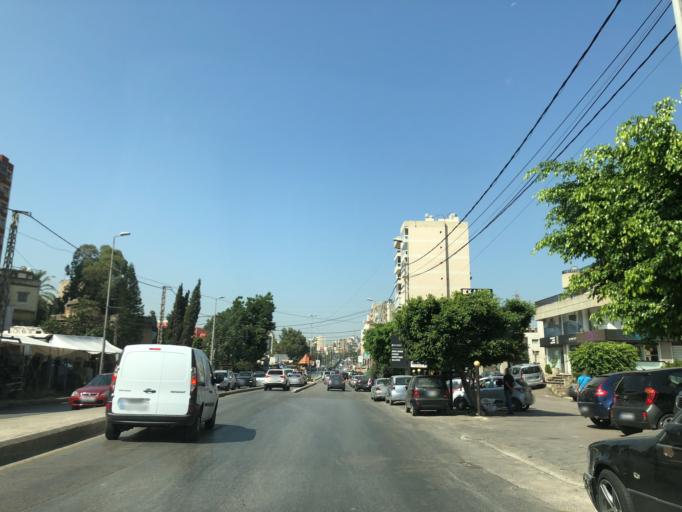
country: LB
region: Mont-Liban
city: Jdaidet el Matn
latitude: 33.8827
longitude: 35.5553
